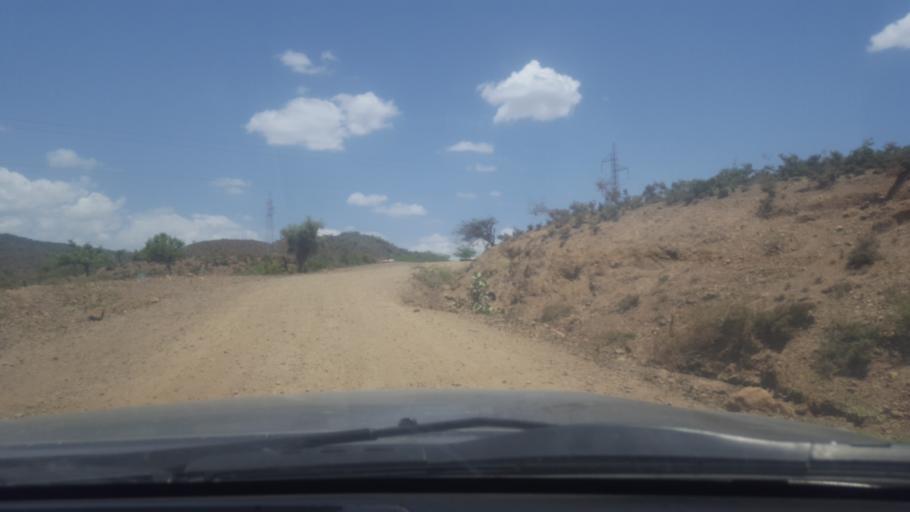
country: ET
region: Oromiya
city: Deder
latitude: 9.5438
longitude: 41.4494
